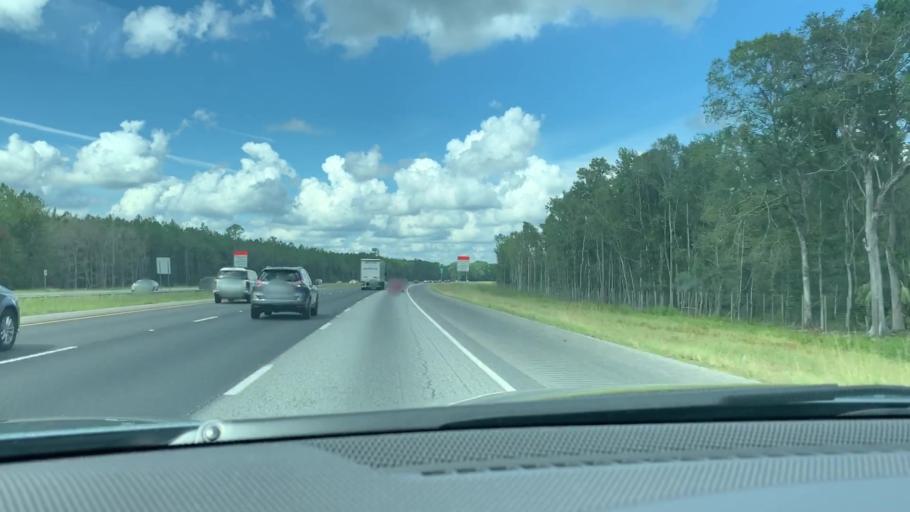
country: US
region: Georgia
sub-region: Camden County
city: Kingsland
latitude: 30.8702
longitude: -81.6833
